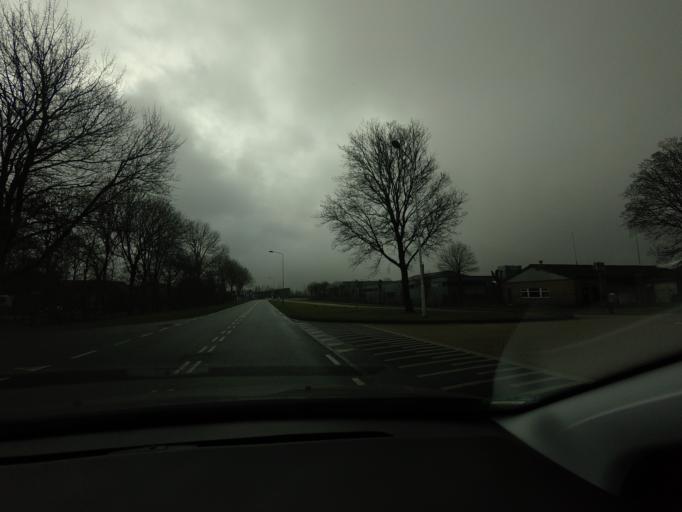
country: NL
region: Friesland
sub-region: Sudwest Fryslan
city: Makkum
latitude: 53.0539
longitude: 5.4100
